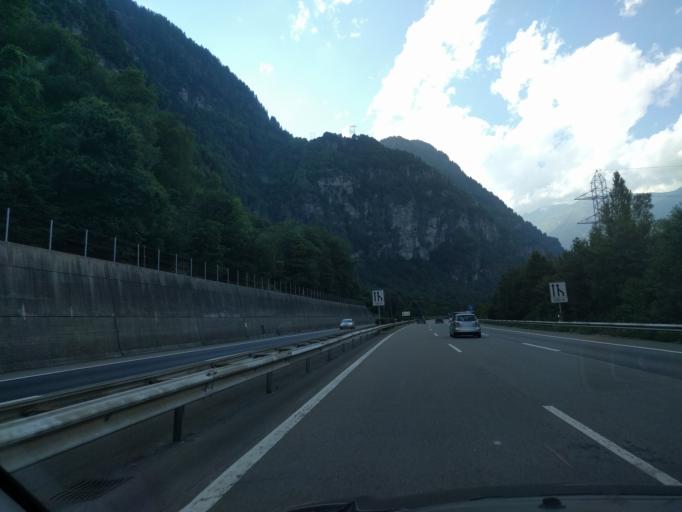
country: CH
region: Ticino
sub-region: Leventina District
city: Faido
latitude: 46.4403
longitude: 8.8370
